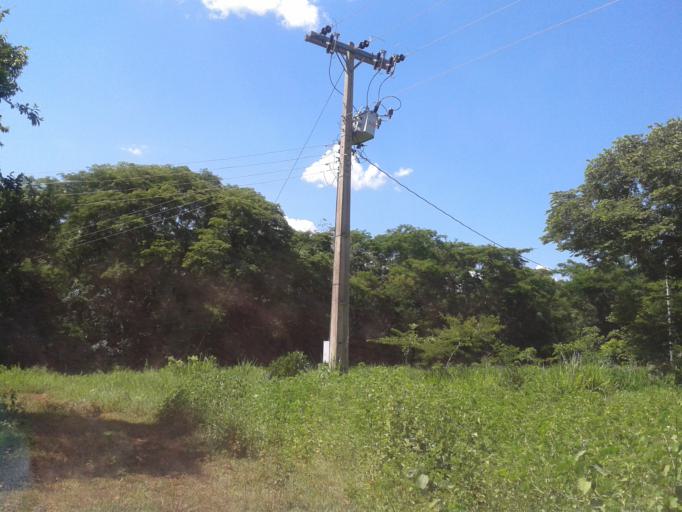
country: BR
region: Minas Gerais
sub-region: Santa Vitoria
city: Santa Vitoria
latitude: -19.0984
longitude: -50.5304
